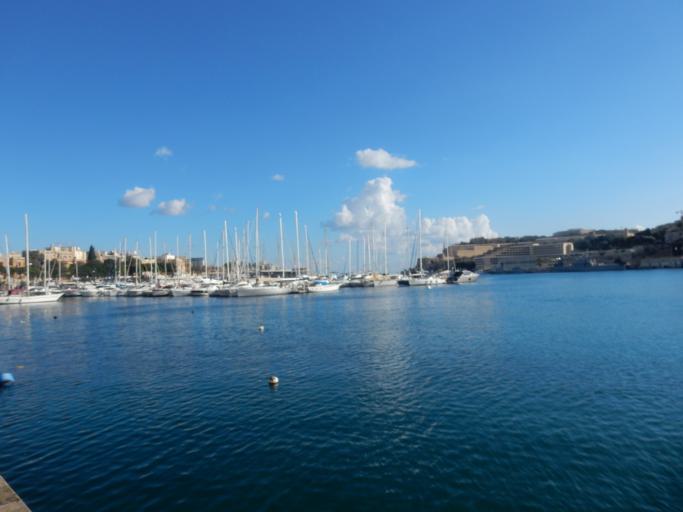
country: MT
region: Tal-Pieta
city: Pieta
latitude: 35.8954
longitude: 14.4973
